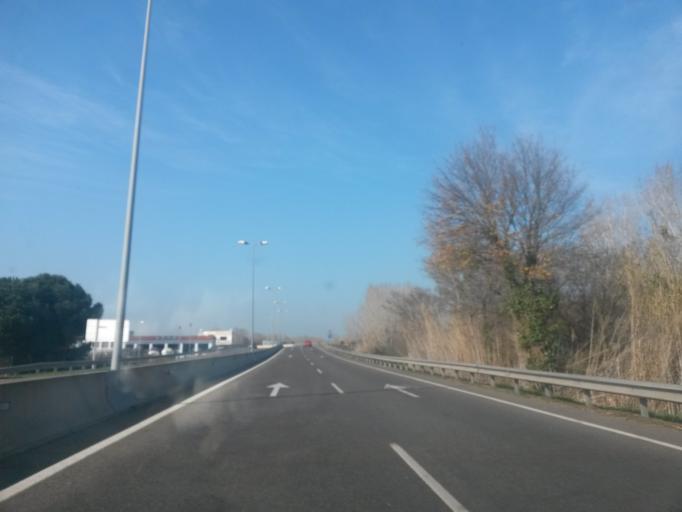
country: ES
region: Catalonia
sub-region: Provincia de Girona
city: Castello d'Empuries
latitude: 42.2532
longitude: 3.0732
